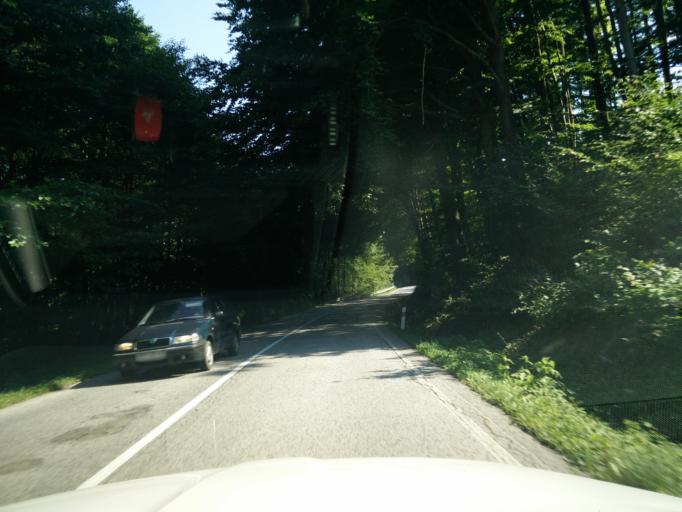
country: SK
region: Nitriansky
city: Bojnice
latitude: 48.8596
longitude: 18.4620
